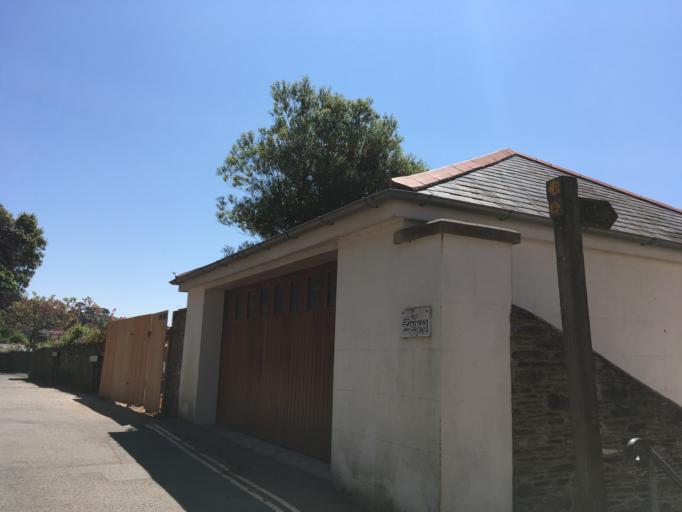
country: GB
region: England
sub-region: Devon
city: Dartmouth
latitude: 50.3477
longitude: -3.5704
